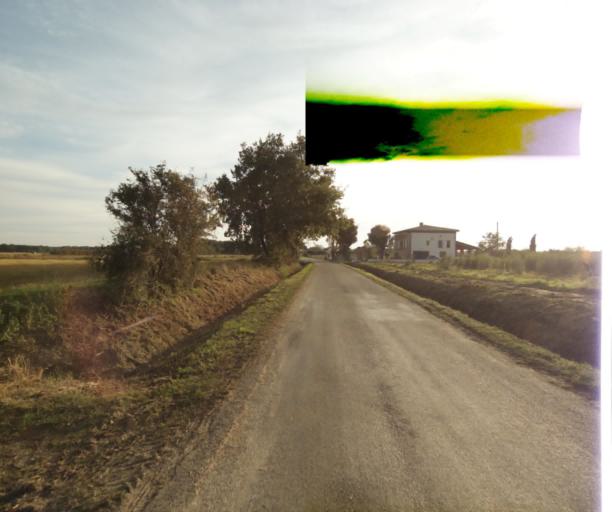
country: FR
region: Midi-Pyrenees
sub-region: Departement du Tarn-et-Garonne
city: Labastide-Saint-Pierre
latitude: 43.8961
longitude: 1.3583
